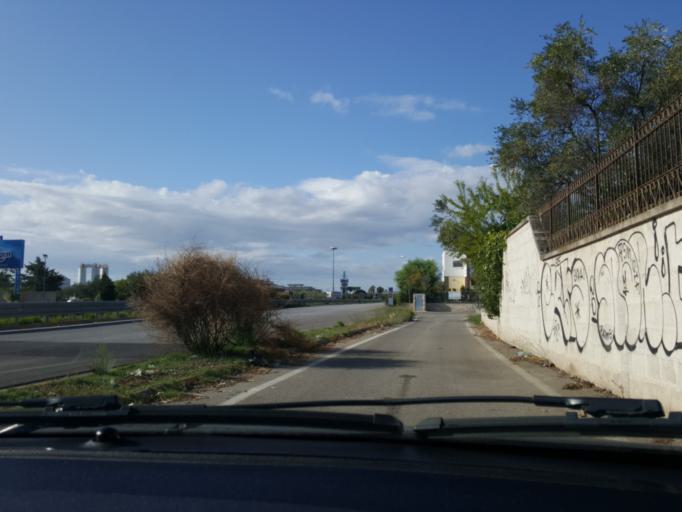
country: IT
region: Apulia
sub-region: Provincia di Bari
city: Triggiano
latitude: 41.0886
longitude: 16.9488
